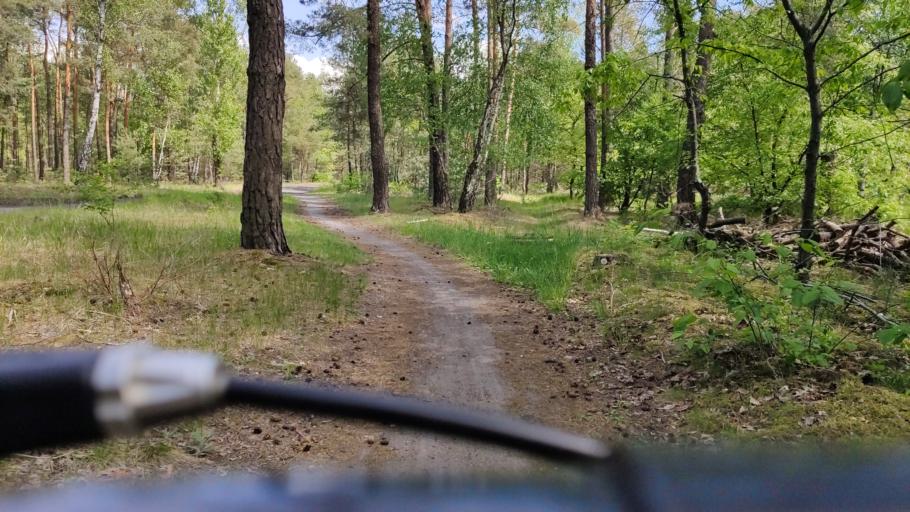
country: PL
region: Kujawsko-Pomorskie
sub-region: Wloclawek
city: Wloclawek
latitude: 52.6356
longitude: 19.1209
